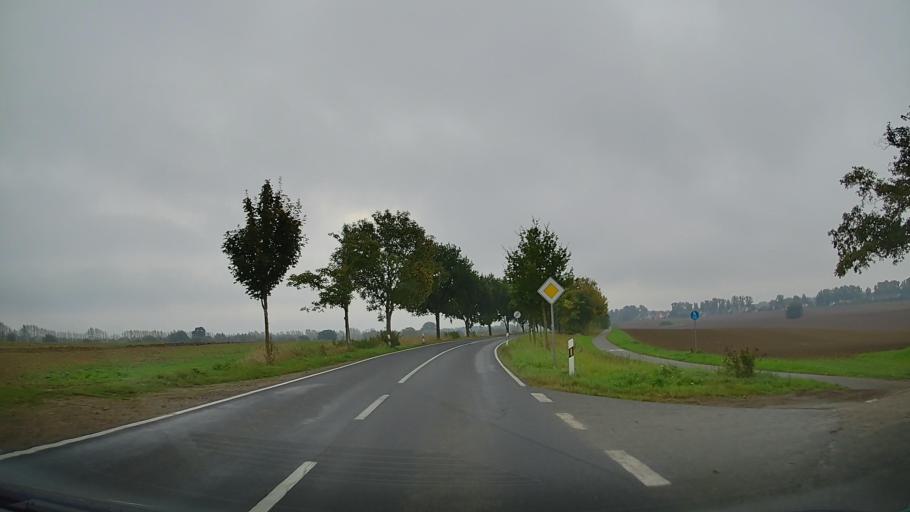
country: DE
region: Mecklenburg-Vorpommern
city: Ostseebad Boltenhagen
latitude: 53.9518
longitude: 11.2296
